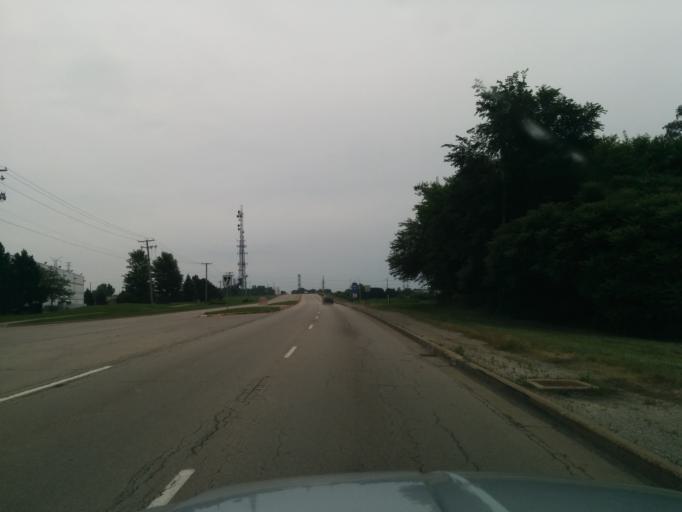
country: US
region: Illinois
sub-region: DuPage County
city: Warrenville
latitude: 41.8044
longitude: -88.2395
